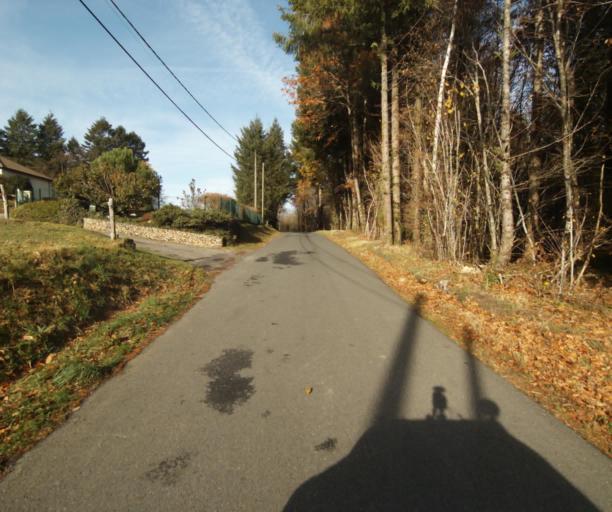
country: FR
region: Limousin
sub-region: Departement de la Correze
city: Sainte-Fortunade
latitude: 45.2158
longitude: 1.7526
